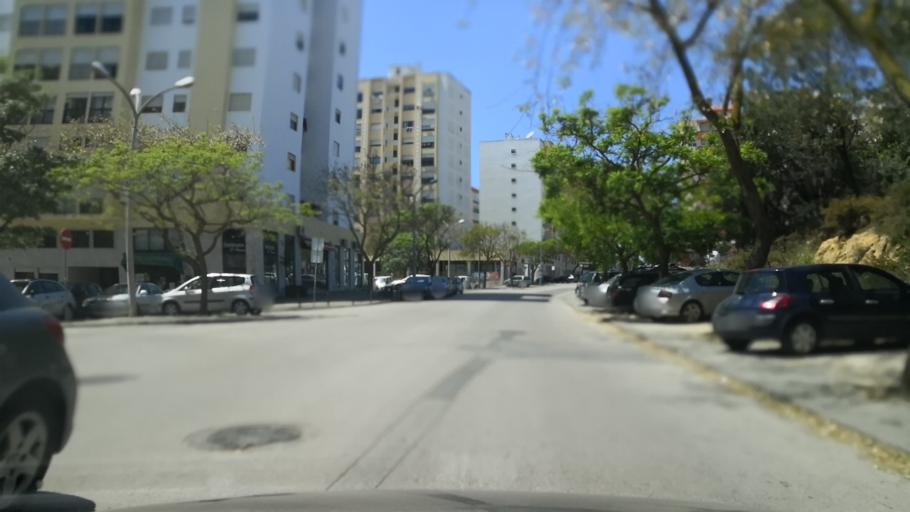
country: PT
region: Setubal
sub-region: Setubal
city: Setubal
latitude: 38.5361
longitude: -8.8688
